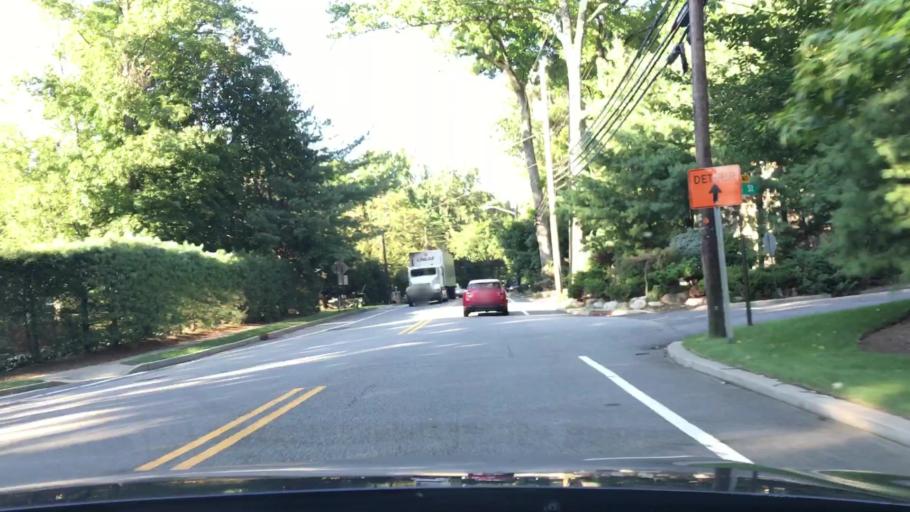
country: US
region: New Jersey
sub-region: Bergen County
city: Closter
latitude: 40.9804
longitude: -73.9433
